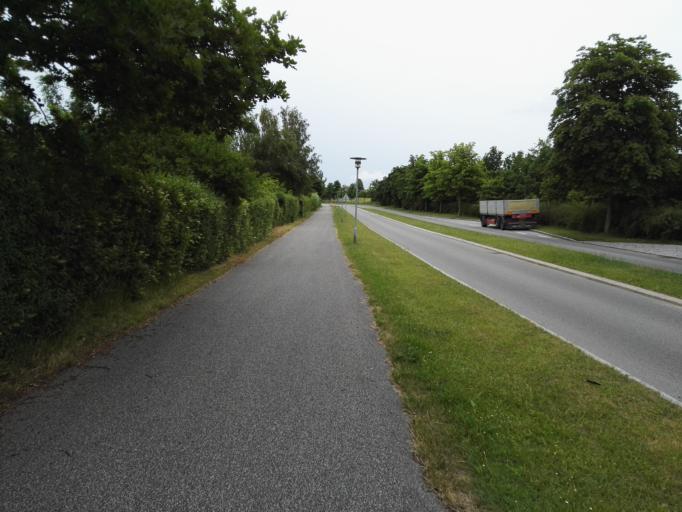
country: DK
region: Capital Region
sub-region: Egedal Kommune
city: Vekso
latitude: 55.7506
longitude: 12.2404
